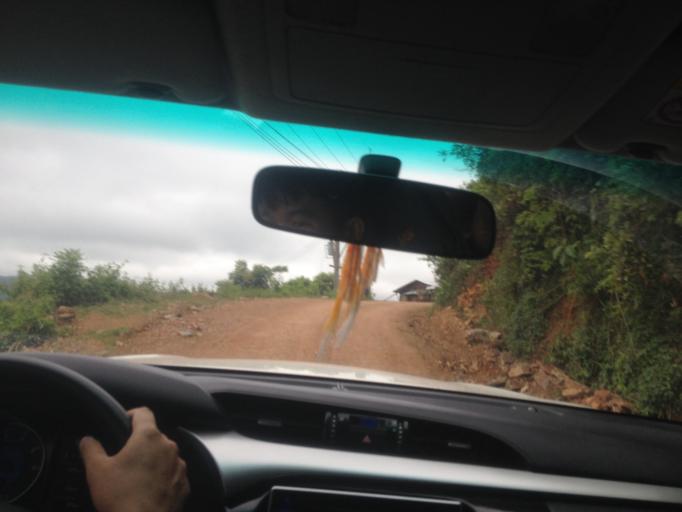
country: TH
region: Nan
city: Chaloem Phra Kiat
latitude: 19.9746
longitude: 101.1359
